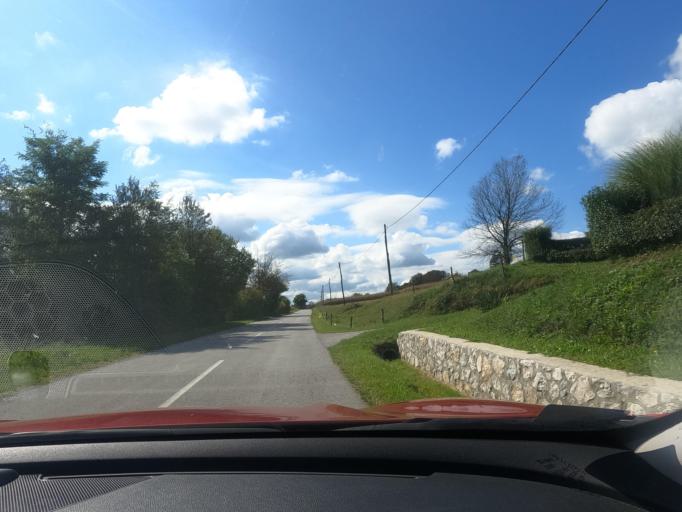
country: BA
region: Federation of Bosnia and Herzegovina
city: Velika Kladusa
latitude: 45.2165
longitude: 15.8244
